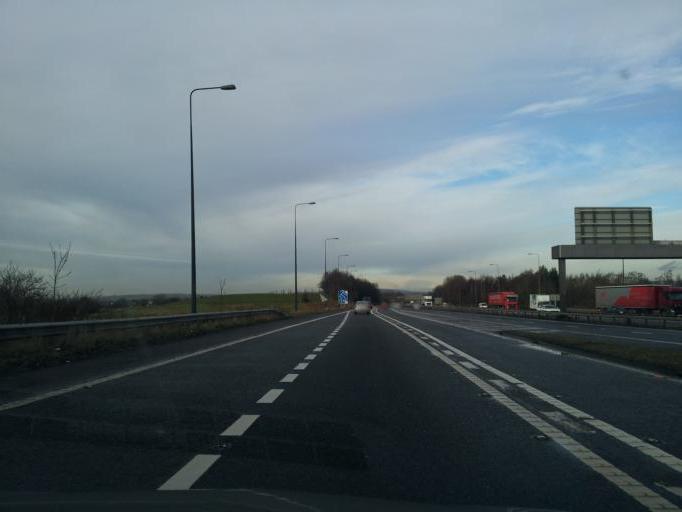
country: GB
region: England
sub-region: Borough of Bury
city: Prestwich
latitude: 53.5522
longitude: -2.2635
